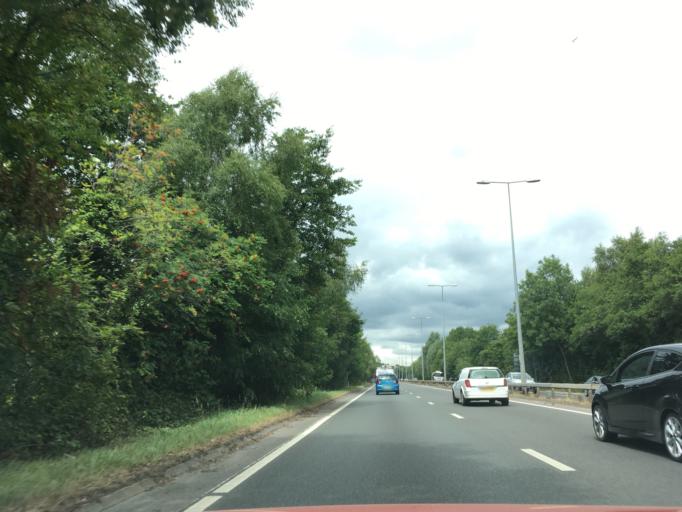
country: GB
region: Wales
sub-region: Torfaen County Borough
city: New Inn
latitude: 51.6822
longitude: -3.0162
